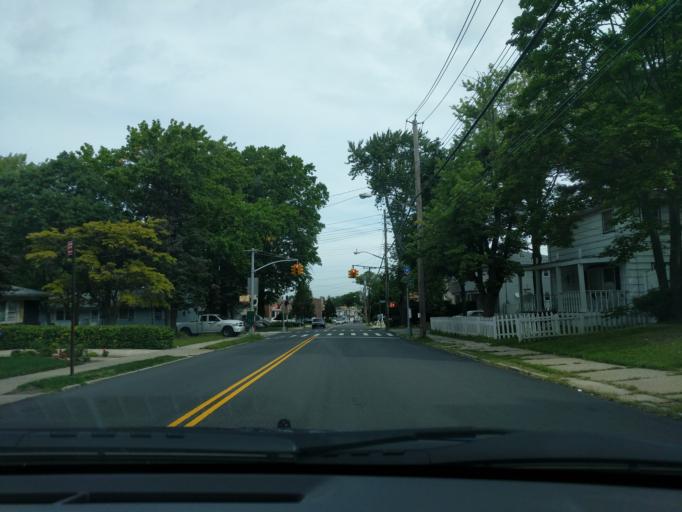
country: US
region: New York
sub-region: Richmond County
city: Bloomfield
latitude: 40.6098
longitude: -74.1323
